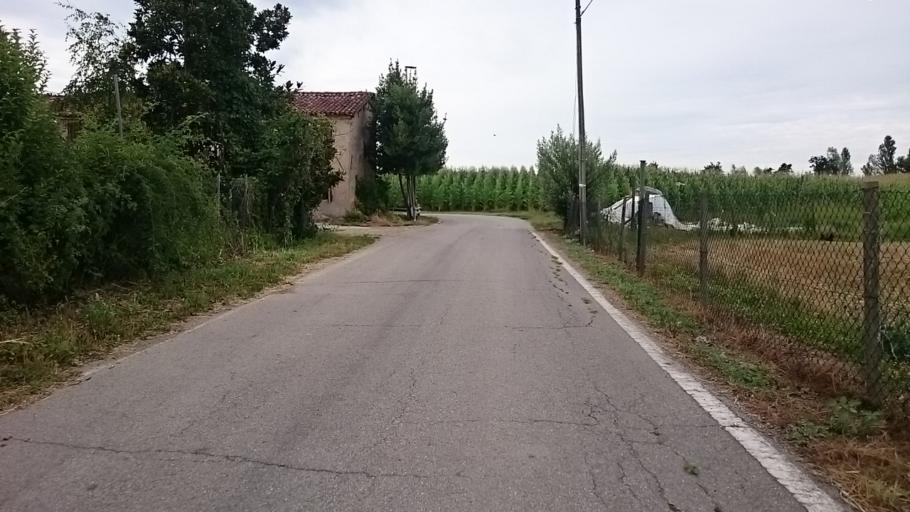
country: IT
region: Veneto
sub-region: Provincia di Padova
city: Terradura
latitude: 45.3235
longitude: 11.8389
